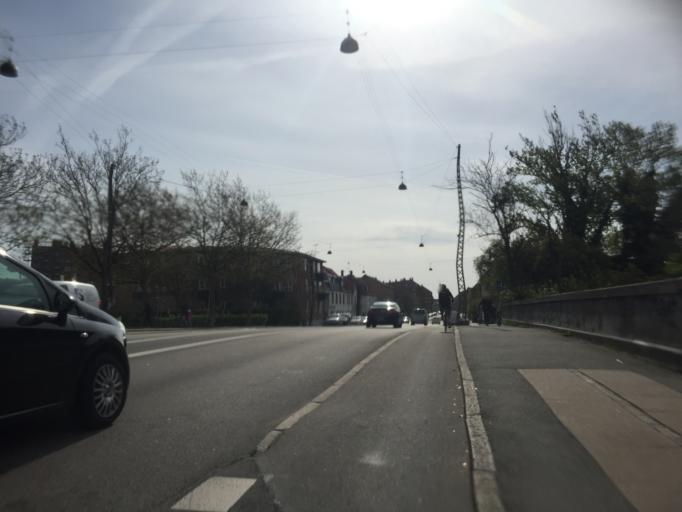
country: DK
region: Capital Region
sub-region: Kobenhavn
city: Vanlose
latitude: 55.6693
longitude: 12.4933
